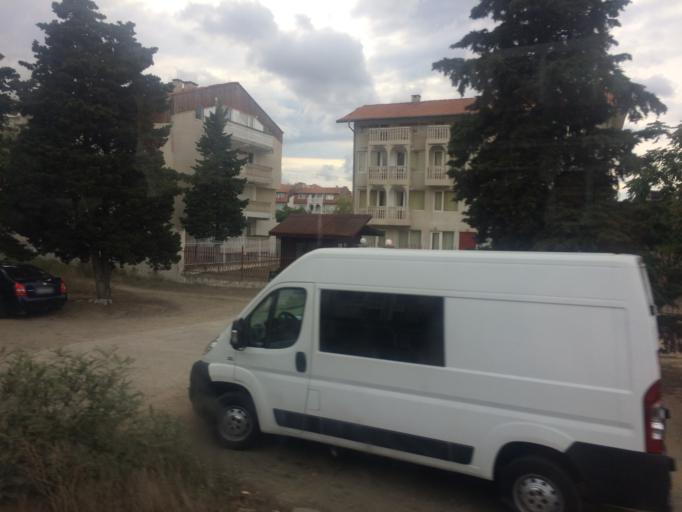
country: BG
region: Burgas
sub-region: Obshtina Nesebur
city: Sveti Vlas
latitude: 42.7028
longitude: 27.7152
